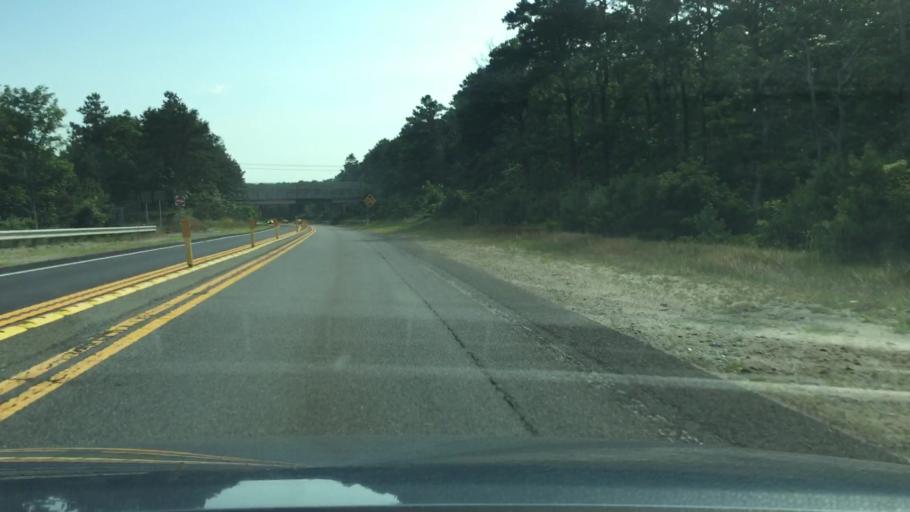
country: US
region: Massachusetts
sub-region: Barnstable County
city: East Harwich
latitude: 41.7382
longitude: -70.0207
